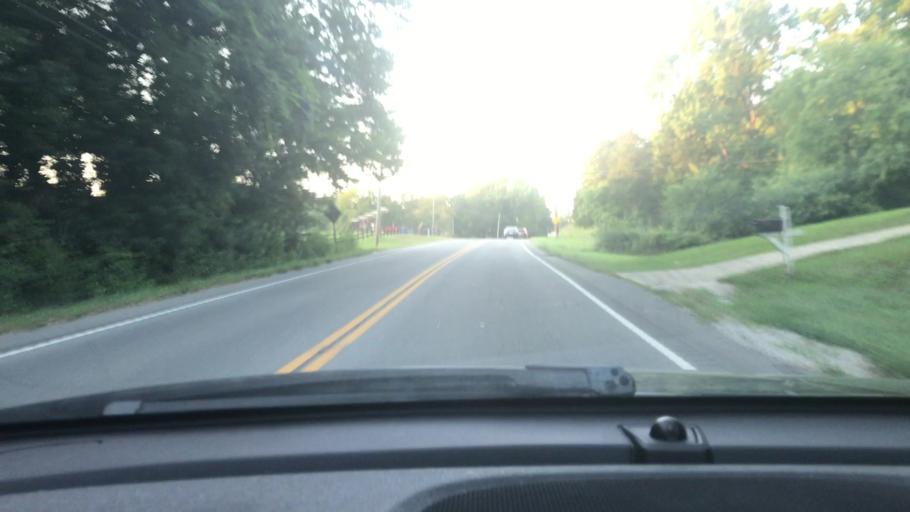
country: US
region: Tennessee
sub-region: Dickson County
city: Dickson
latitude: 36.1034
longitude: -87.3740
